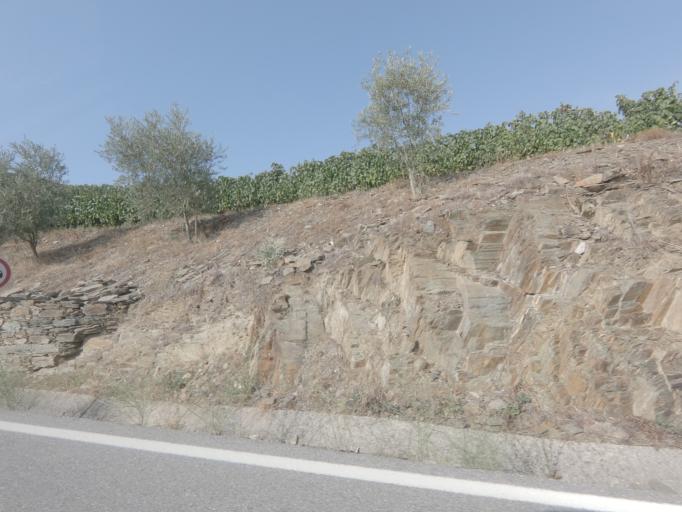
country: PT
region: Viseu
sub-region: Tabuaco
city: Tabuaco
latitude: 41.1401
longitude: -7.5417
